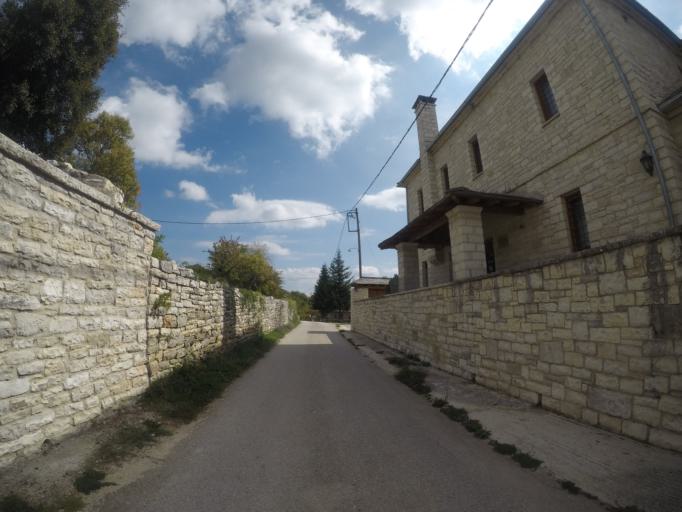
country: GR
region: Epirus
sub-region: Nomos Ioanninon
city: Asprangeloi
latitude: 39.8812
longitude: 20.7466
